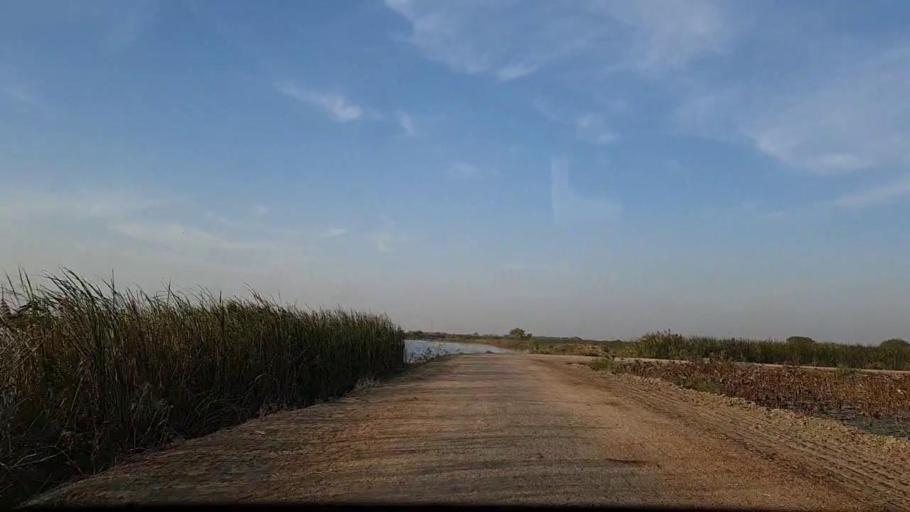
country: PK
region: Sindh
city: Mirpur Batoro
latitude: 24.6568
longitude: 68.1464
